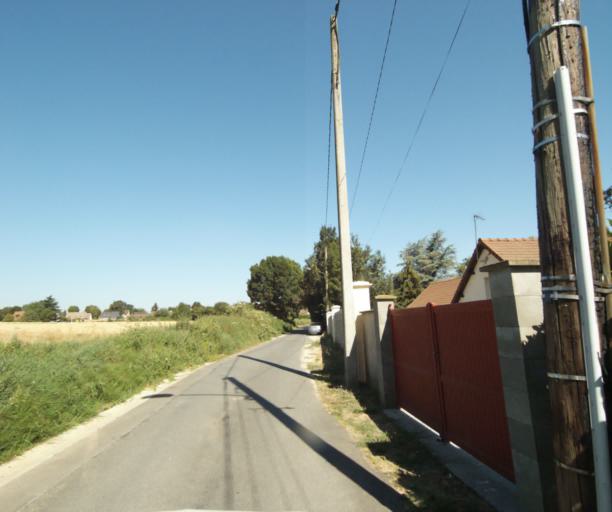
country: FR
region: Ile-de-France
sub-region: Departement de l'Essonne
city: Itteville
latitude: 48.5329
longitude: 2.3551
